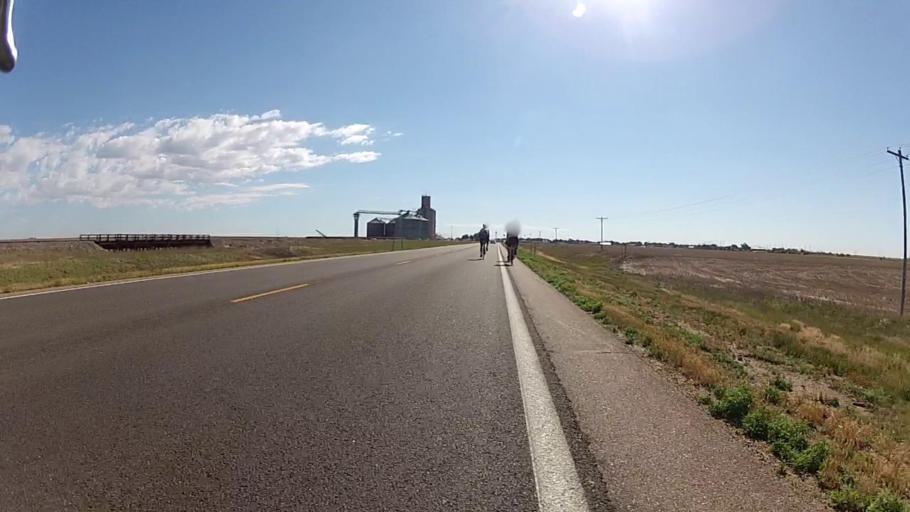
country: US
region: Kansas
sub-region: Gray County
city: Cimarron
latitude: 37.5939
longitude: -100.4620
